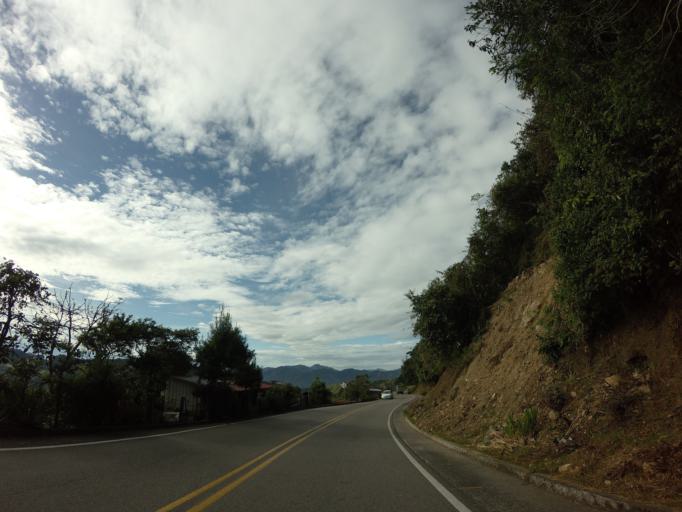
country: CO
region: Tolima
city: Herveo
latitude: 5.1404
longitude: -75.1440
